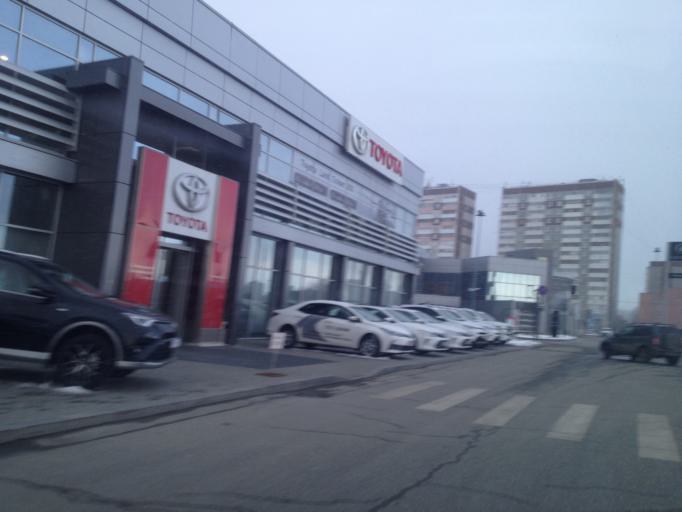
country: RU
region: Sverdlovsk
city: Shirokaya Rechka
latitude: 56.8279
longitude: 60.5264
